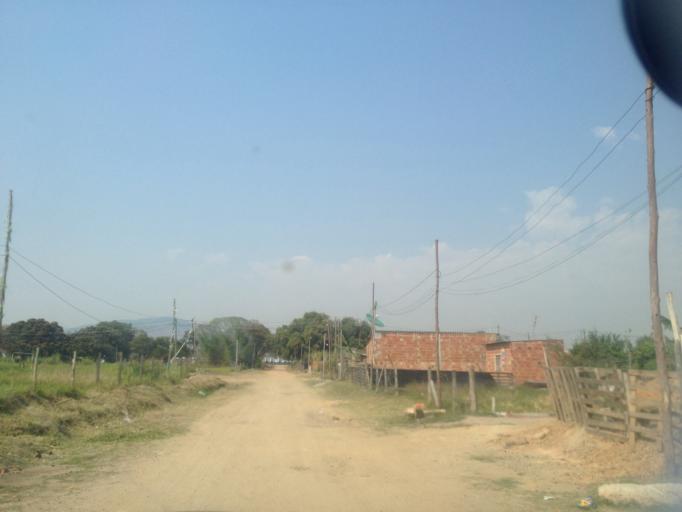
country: BR
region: Rio de Janeiro
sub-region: Porto Real
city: Porto Real
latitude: -22.4310
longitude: -44.3410
